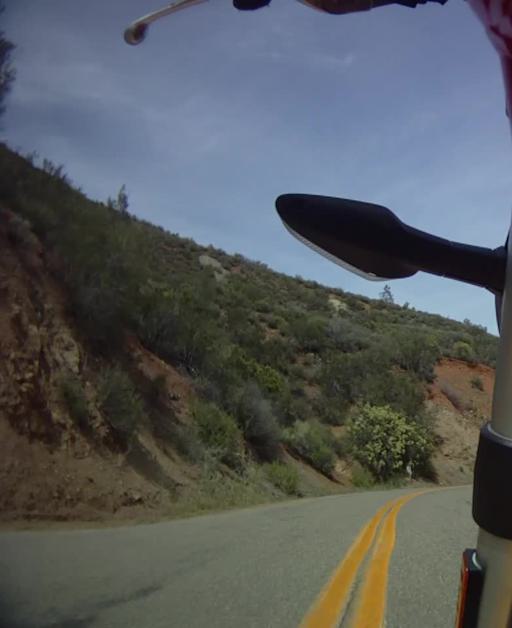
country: US
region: California
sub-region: Stanislaus County
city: Patterson
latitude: 37.4052
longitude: -121.4337
